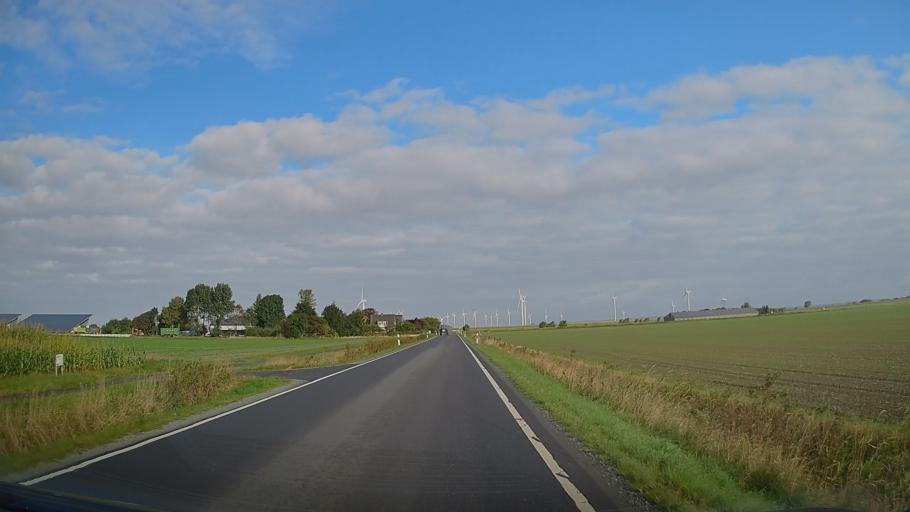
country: DE
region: Schleswig-Holstein
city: Reussenkoge
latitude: 54.5817
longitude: 8.9254
